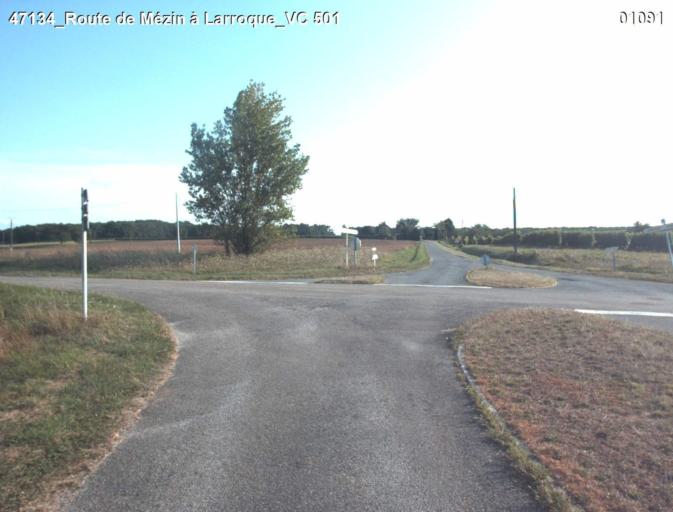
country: FR
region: Aquitaine
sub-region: Departement du Lot-et-Garonne
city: Mezin
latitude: 44.0075
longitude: 0.2760
